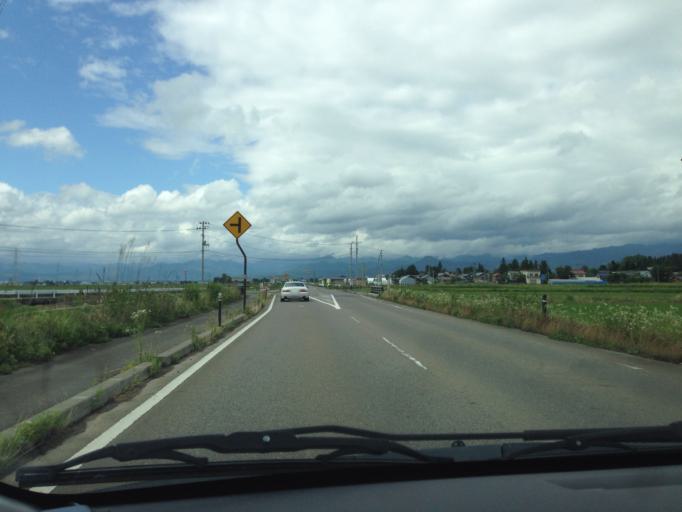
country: JP
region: Fukushima
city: Kitakata
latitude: 37.5944
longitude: 139.9122
